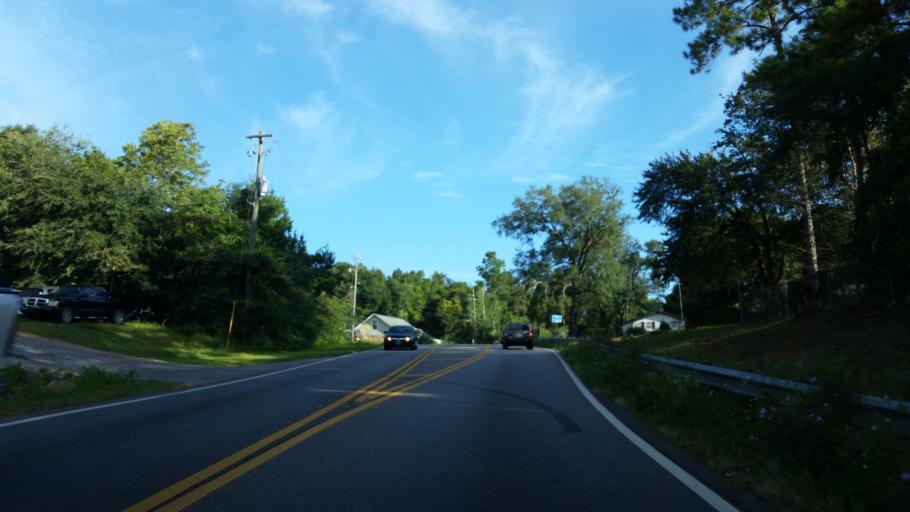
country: US
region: Florida
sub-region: Santa Rosa County
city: Milton
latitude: 30.6159
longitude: -87.0643
